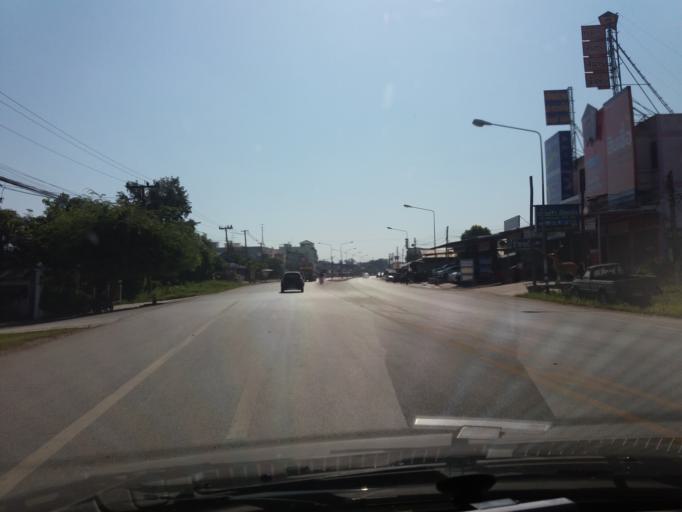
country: TH
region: Kamphaeng Phet
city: Khlong Khlung
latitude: 16.1752
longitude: 99.7937
